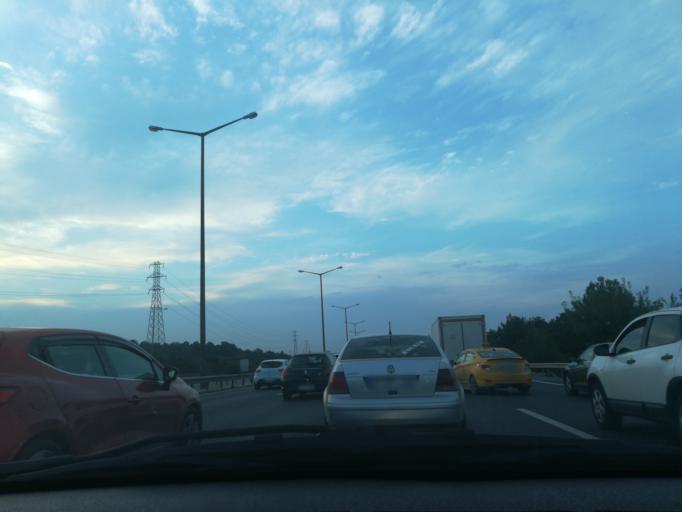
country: TR
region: Istanbul
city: Umraniye
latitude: 41.0589
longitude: 29.1175
